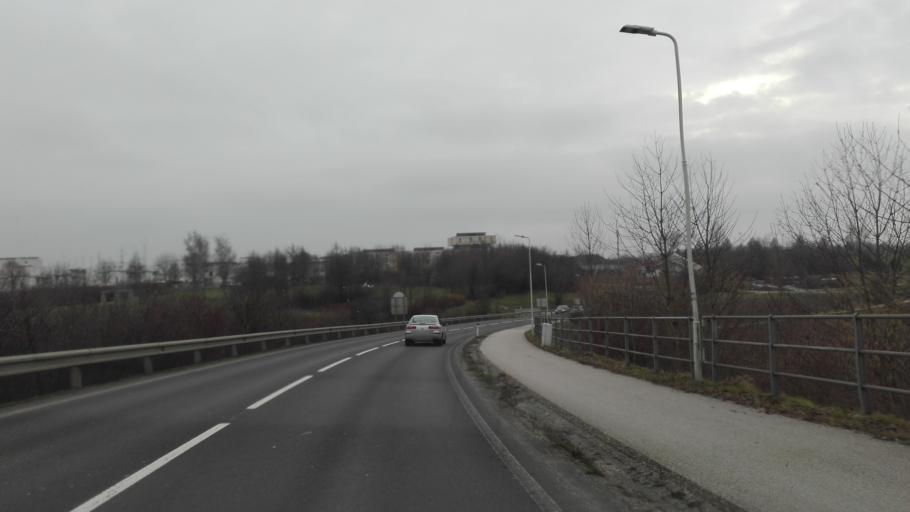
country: AT
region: Upper Austria
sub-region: Politischer Bezirk Linz-Land
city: Leonding
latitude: 48.2726
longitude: 14.2575
